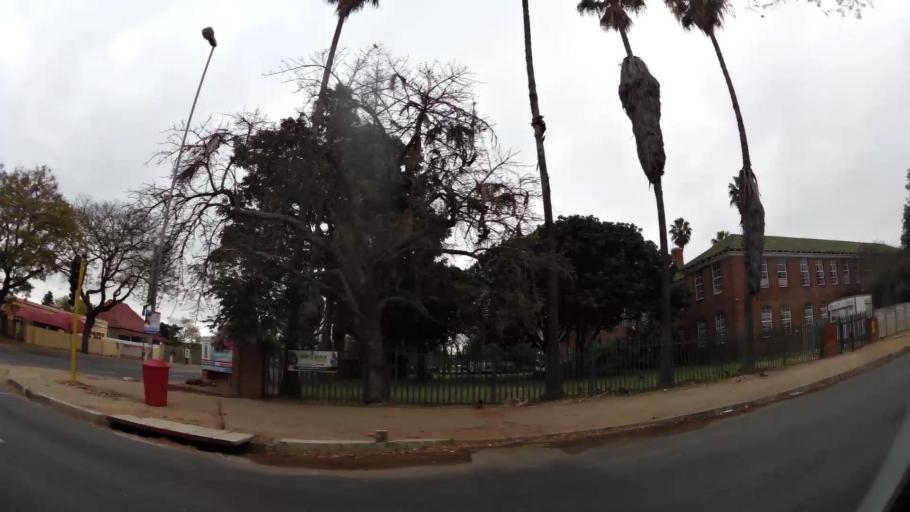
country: ZA
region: Limpopo
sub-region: Capricorn District Municipality
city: Polokwane
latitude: -23.9018
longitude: 29.4549
